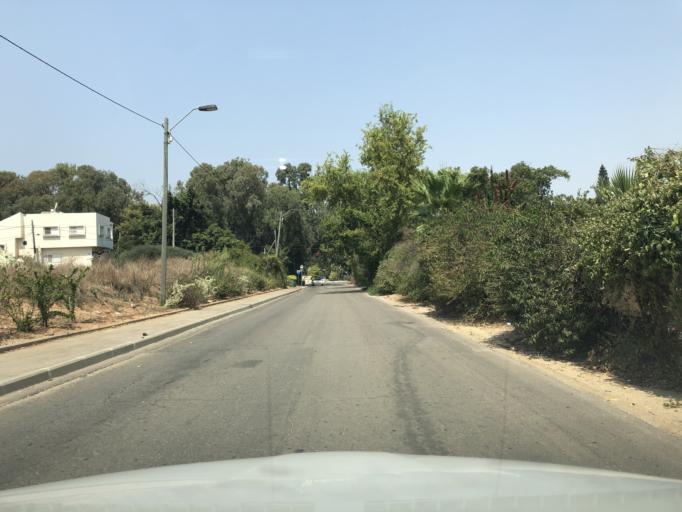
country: IL
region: Central District
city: Ganne Tiqwa
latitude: 32.0675
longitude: 34.8760
